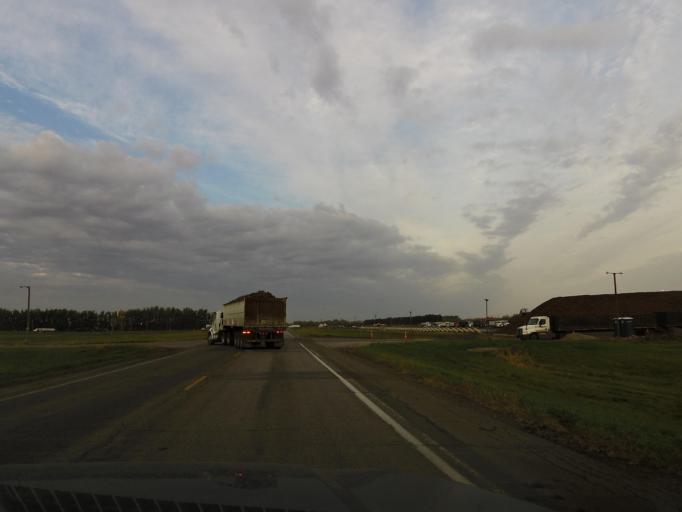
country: US
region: North Dakota
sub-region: Walsh County
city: Grafton
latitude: 48.6010
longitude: -97.4514
